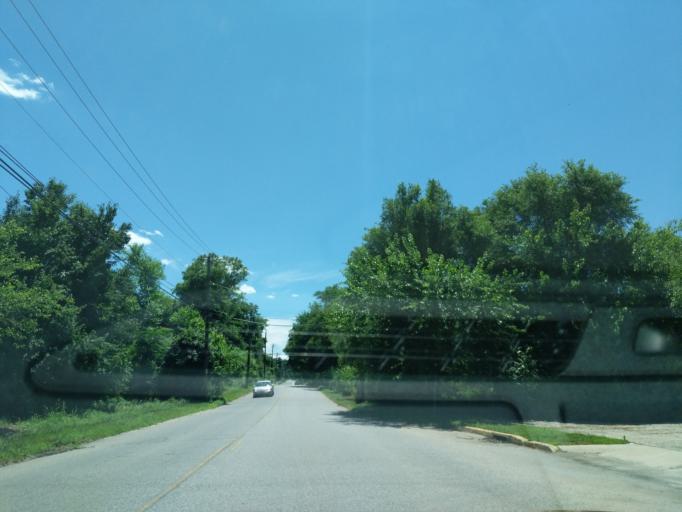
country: US
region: New Jersey
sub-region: Gloucester County
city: Wenonah
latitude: 39.8119
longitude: -75.1263
